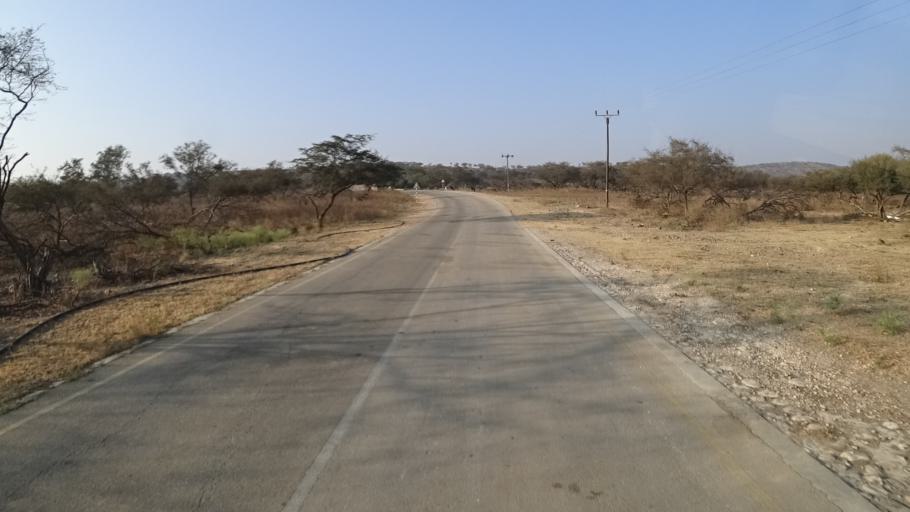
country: YE
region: Al Mahrah
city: Hawf
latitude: 16.7832
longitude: 53.3306
